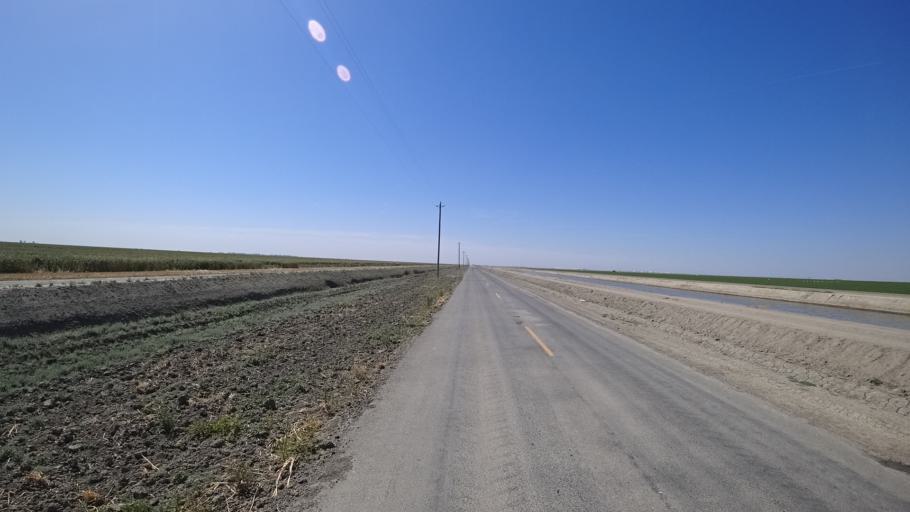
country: US
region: California
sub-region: Kings County
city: Corcoran
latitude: 35.9904
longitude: -119.5362
